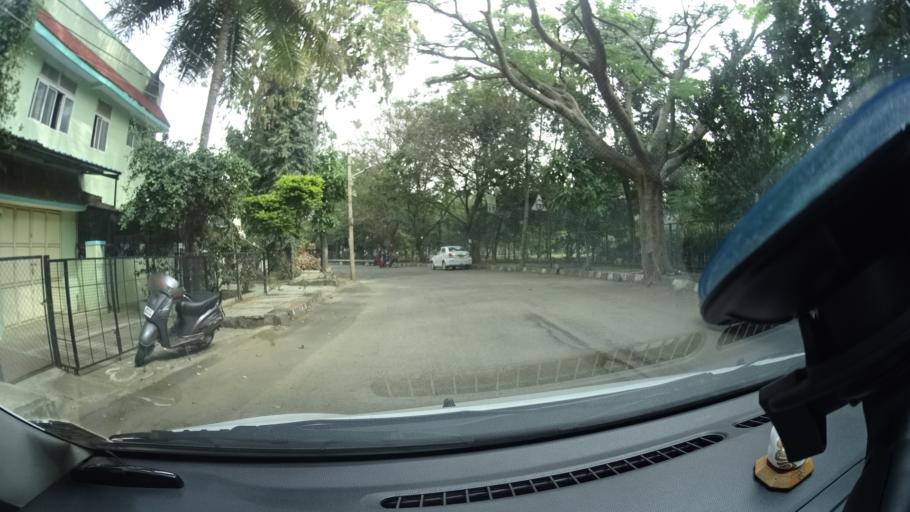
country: IN
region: Karnataka
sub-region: Bangalore Urban
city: Yelahanka
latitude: 13.0995
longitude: 77.5739
